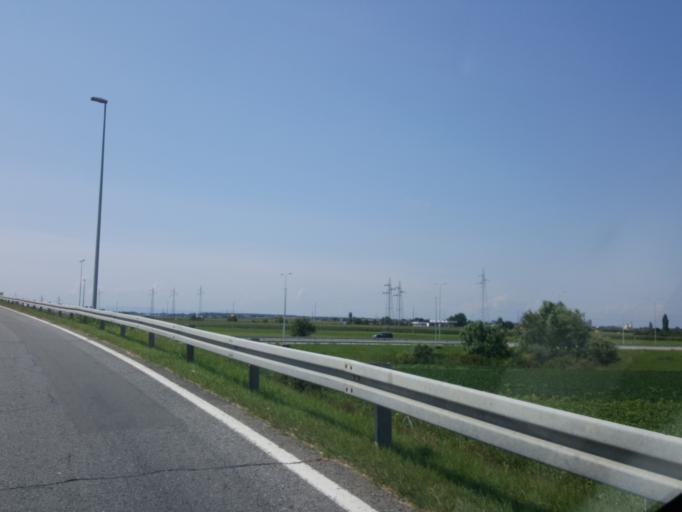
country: RS
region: Autonomna Pokrajina Vojvodina
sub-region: Sremski Okrug
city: Sremska Mitrovica
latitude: 45.0002
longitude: 19.6508
